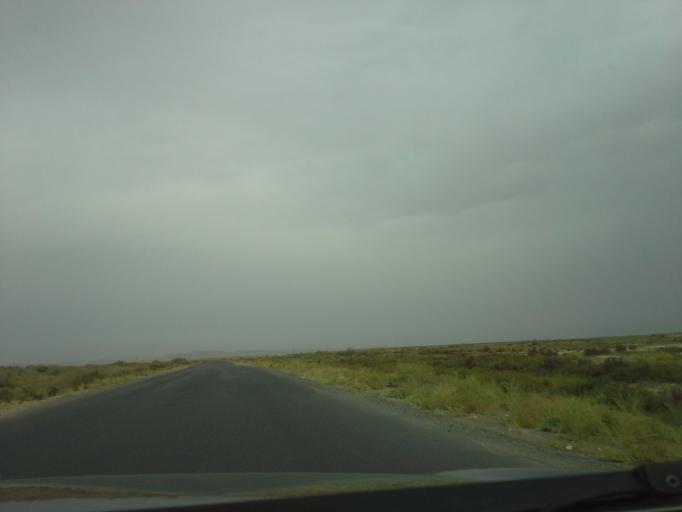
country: AF
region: Jowzjan
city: Khamyab
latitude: 37.7258
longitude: 65.5099
